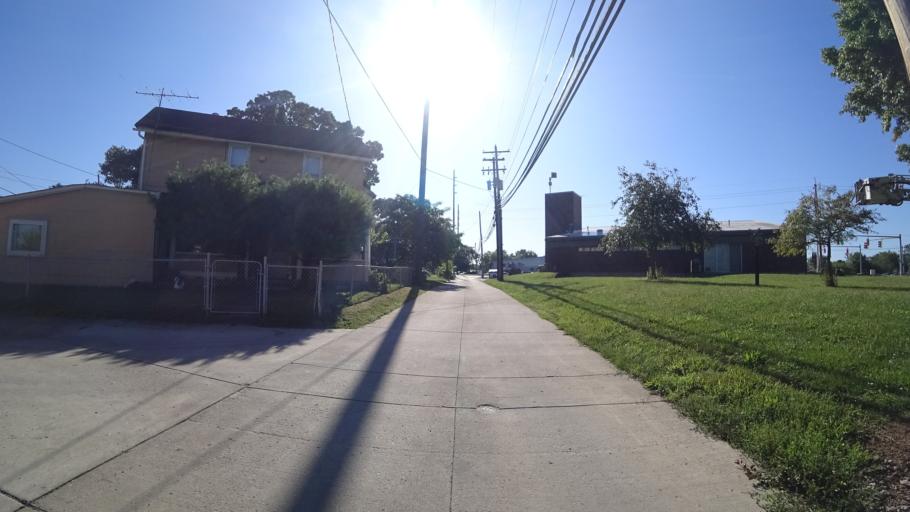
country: US
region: Ohio
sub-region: Butler County
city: Hamilton
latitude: 39.4003
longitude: -84.5456
